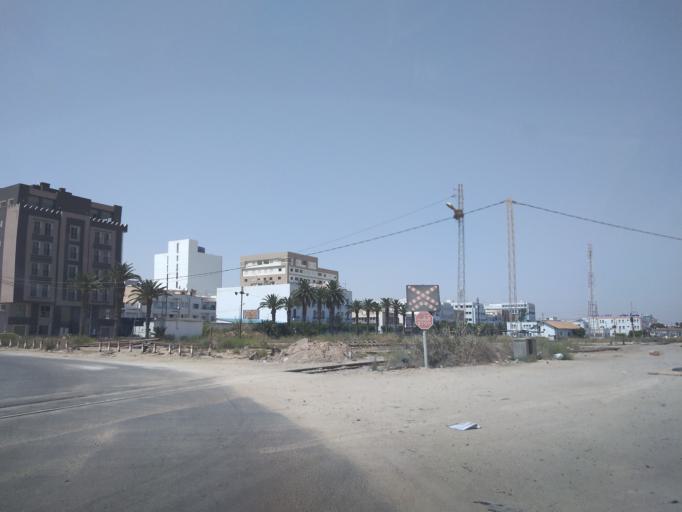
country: TN
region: Safaqis
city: Sfax
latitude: 34.7328
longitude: 10.7696
